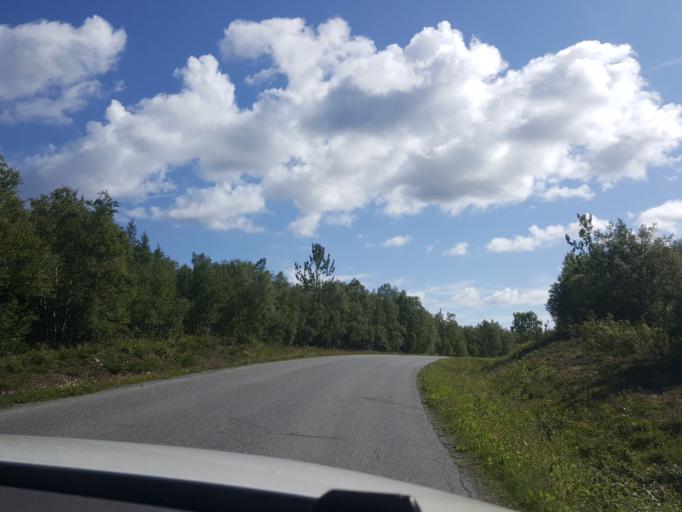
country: NO
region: Nordland
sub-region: Bodo
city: Loding
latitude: 67.2311
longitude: 14.9258
